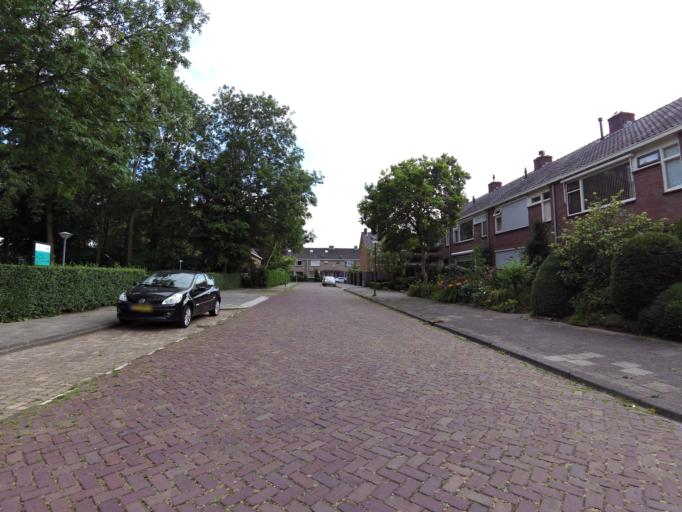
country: NL
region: South Holland
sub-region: Gemeente Dordrecht
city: Dordrecht
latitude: 51.7952
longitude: 4.7122
